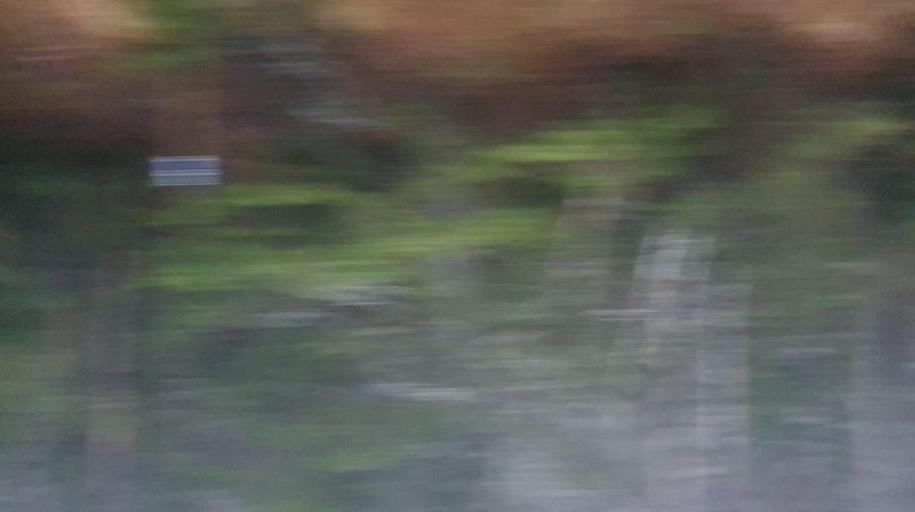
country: NO
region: Buskerud
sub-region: Krodsherad
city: Noresund
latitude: 60.2205
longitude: 9.5338
